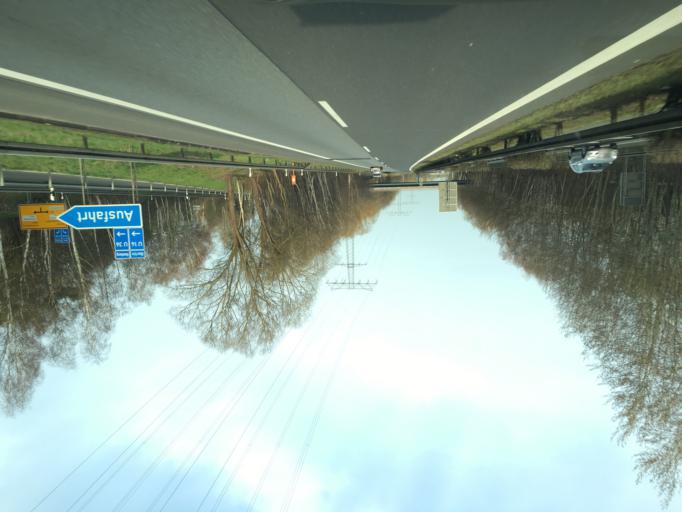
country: DE
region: Brandenburg
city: Birkenwerder
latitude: 52.6999
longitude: 13.2788
